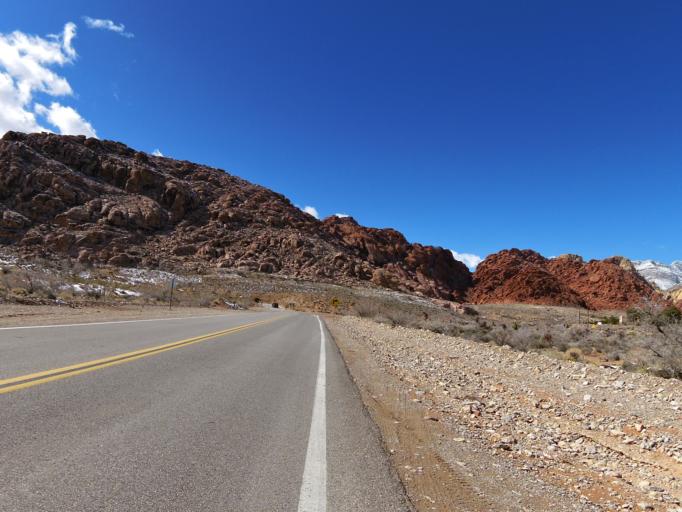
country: US
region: Nevada
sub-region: Clark County
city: Summerlin South
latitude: 36.1475
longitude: -115.4160
